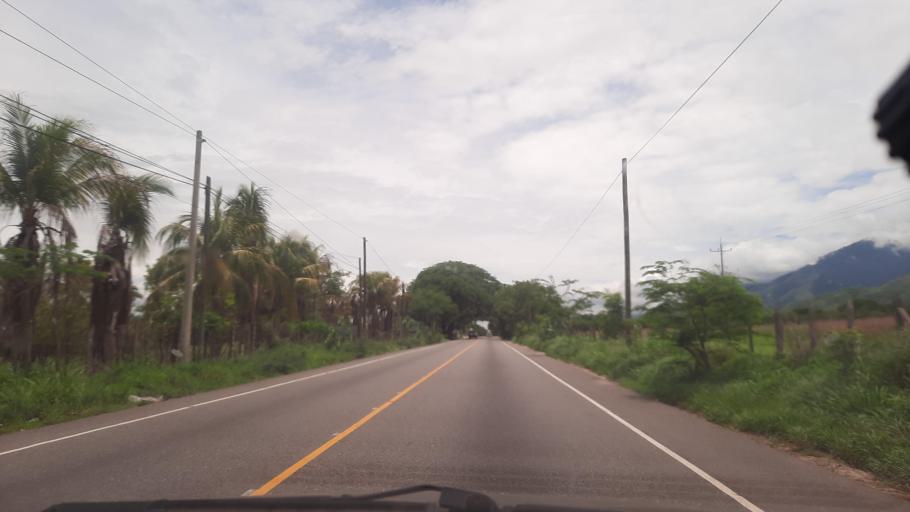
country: GT
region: Zacapa
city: Rio Hondo
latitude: 15.0594
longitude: -89.5431
